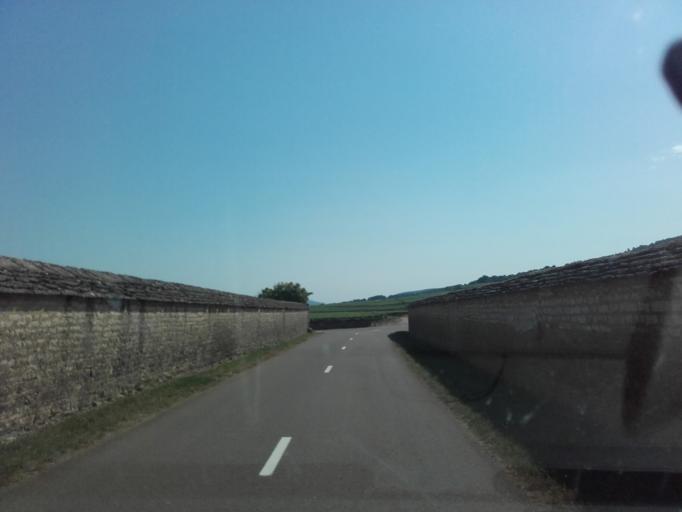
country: FR
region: Bourgogne
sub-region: Departement de la Cote-d'Or
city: Meursault
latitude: 46.9723
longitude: 4.7659
